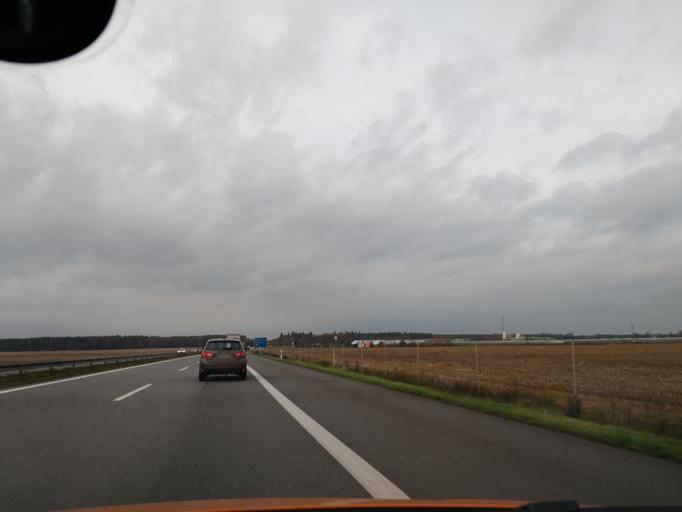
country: DE
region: Brandenburg
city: Wittstock
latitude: 53.0596
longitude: 12.5336
